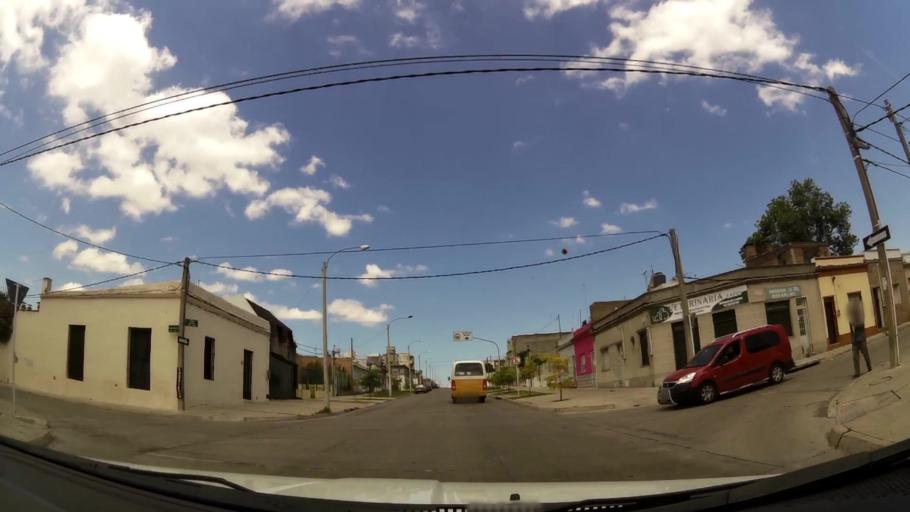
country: UY
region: Montevideo
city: Montevideo
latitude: -34.8506
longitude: -56.2298
